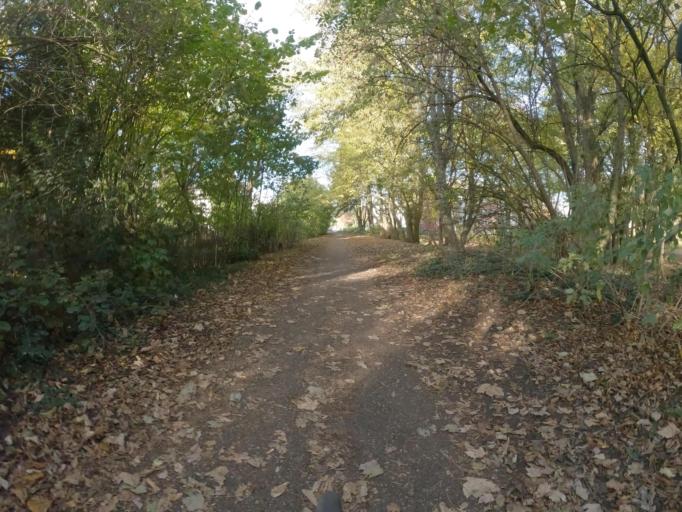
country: NL
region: Limburg
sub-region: Gemeente Kerkrade
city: Kerkrade
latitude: 50.8260
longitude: 6.0872
